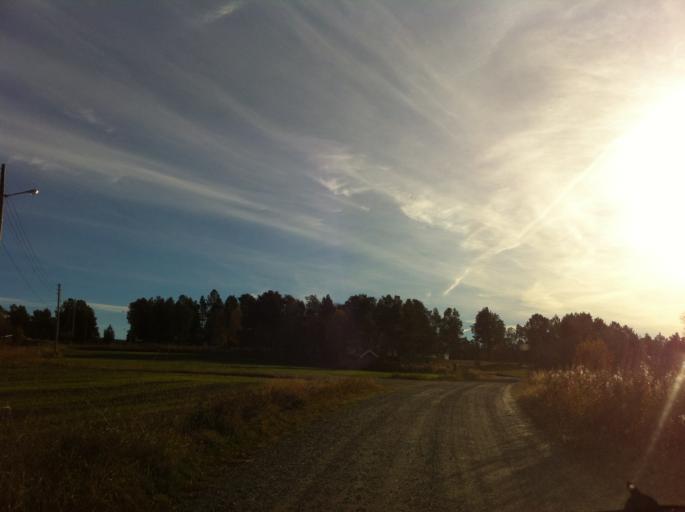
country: NO
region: Hedmark
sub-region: Engerdal
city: Engerdal
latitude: 62.1683
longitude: 11.9422
